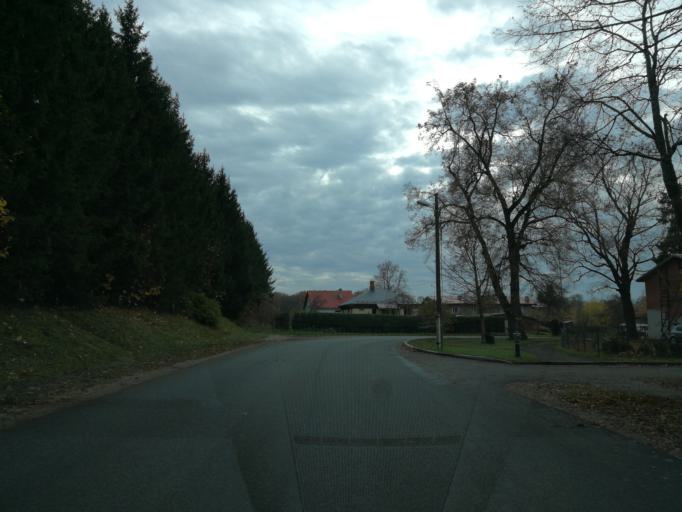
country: LV
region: Cesu Rajons
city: Cesis
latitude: 57.3054
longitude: 25.2749
